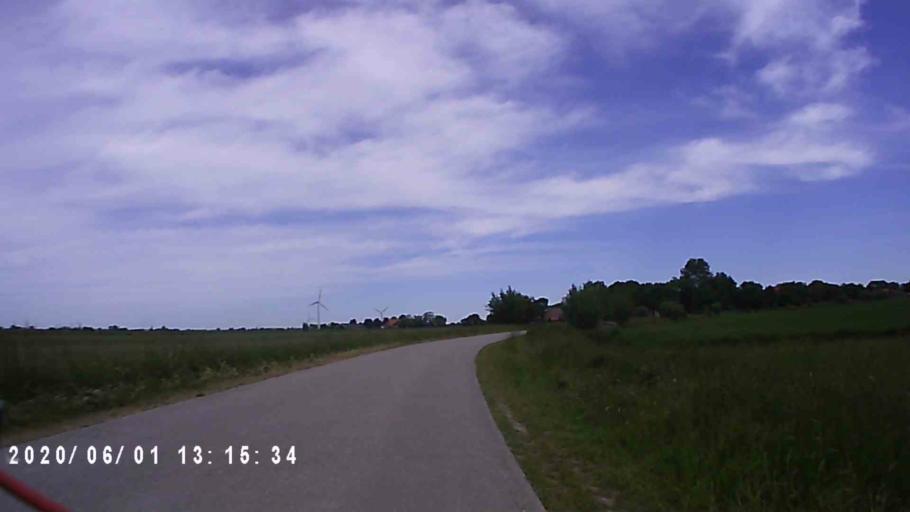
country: NL
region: Friesland
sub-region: Gemeente Littenseradiel
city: Wommels
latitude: 53.1197
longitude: 5.5625
